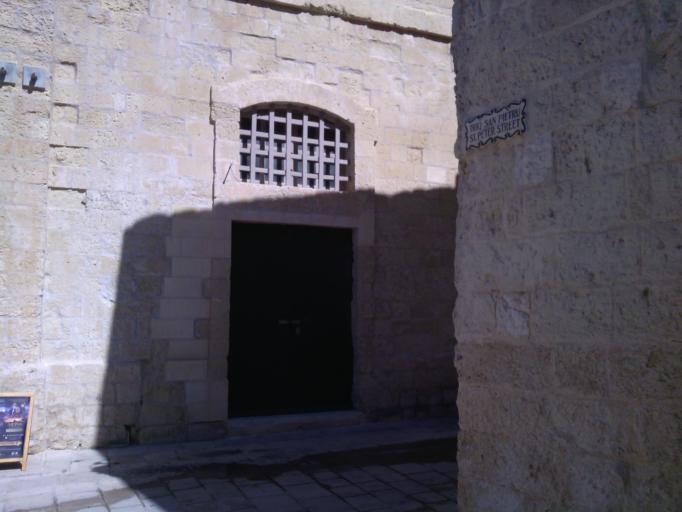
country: MT
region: L-Imdina
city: Imdina
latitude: 35.8867
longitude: 14.4021
